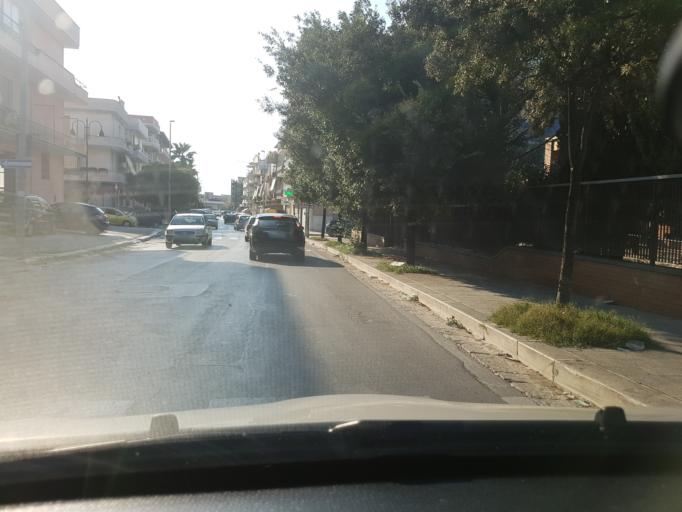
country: IT
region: Apulia
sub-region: Provincia di Foggia
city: Cerignola
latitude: 41.2704
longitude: 15.8981
